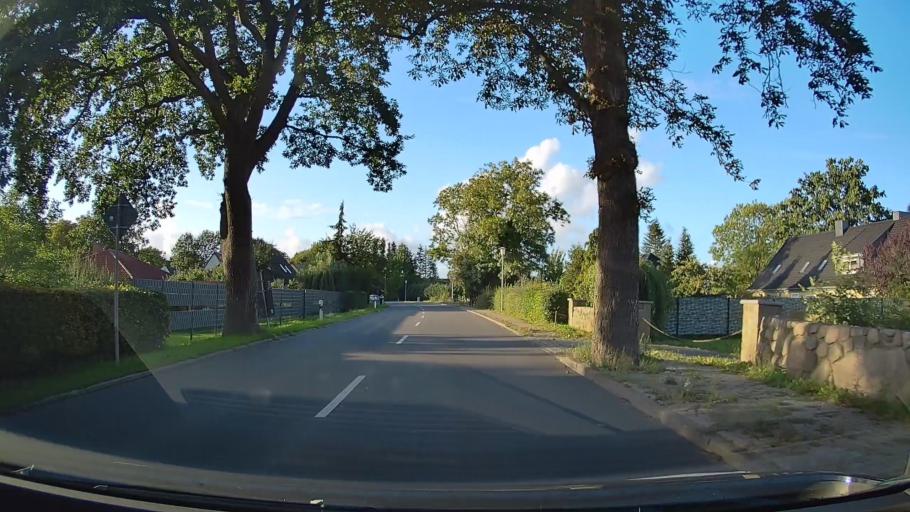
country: DE
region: Mecklenburg-Vorpommern
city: Steinhagen
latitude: 54.1914
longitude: 13.0202
